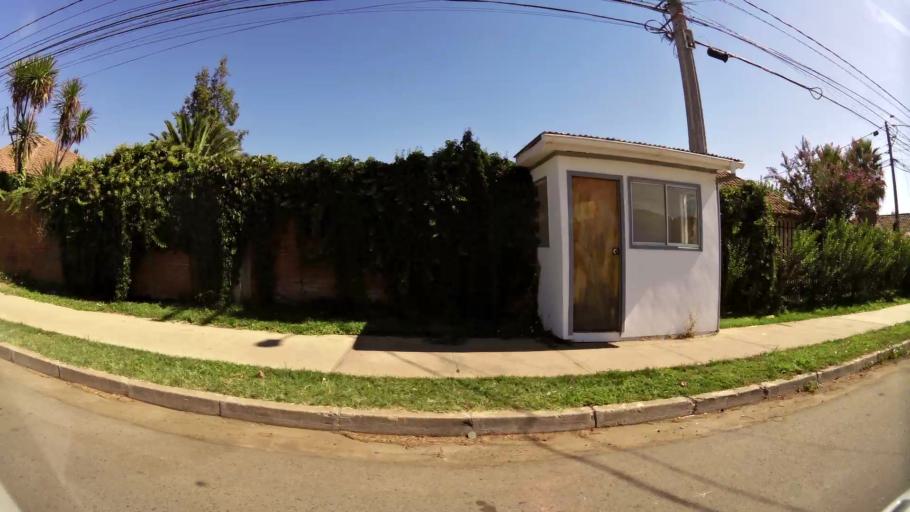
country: CL
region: Maule
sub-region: Provincia de Talca
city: Talca
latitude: -35.4309
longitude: -71.6158
